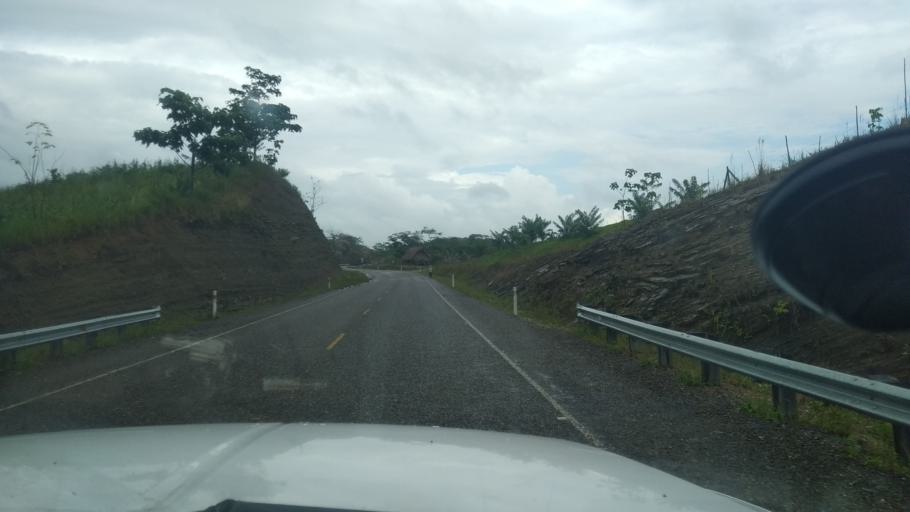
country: GT
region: Peten
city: San Luis
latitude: 16.1840
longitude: -89.1985
